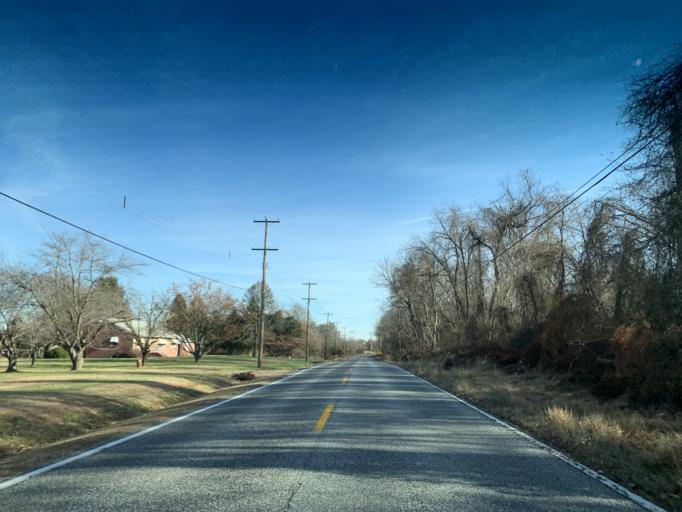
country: US
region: Maryland
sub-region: Cecil County
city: Charlestown
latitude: 39.5798
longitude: -76.0022
